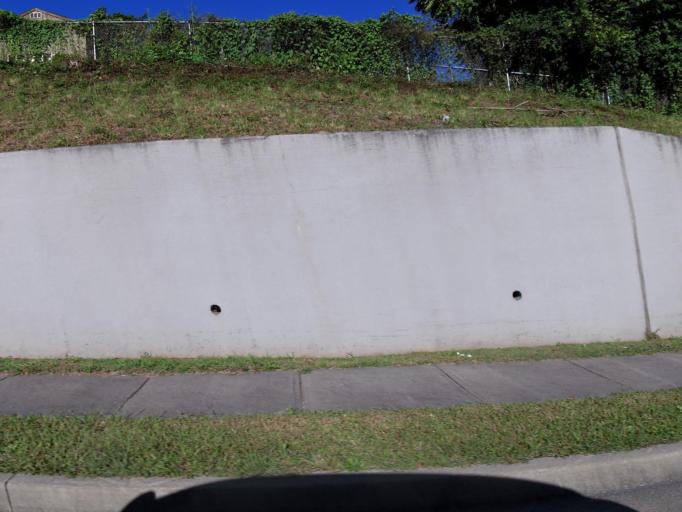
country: US
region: Kentucky
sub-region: Whitley County
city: Williamsburg
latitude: 36.7530
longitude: -84.1579
